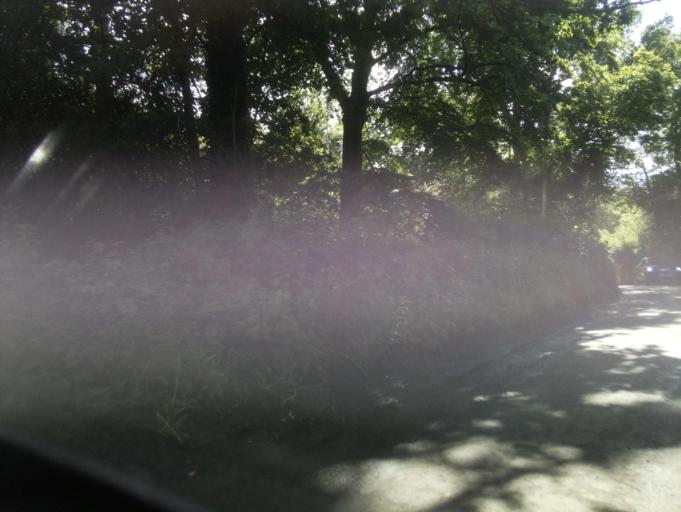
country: GB
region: England
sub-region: Hertfordshire
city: Chorleywood
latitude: 51.6563
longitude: -0.4607
